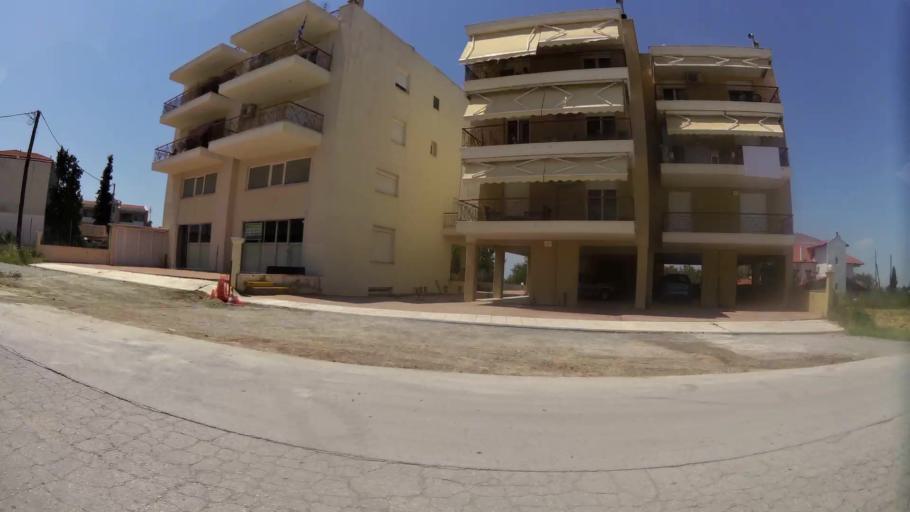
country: GR
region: Central Macedonia
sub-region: Nomos Thessalonikis
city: Epanomi
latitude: 40.4264
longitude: 22.9350
